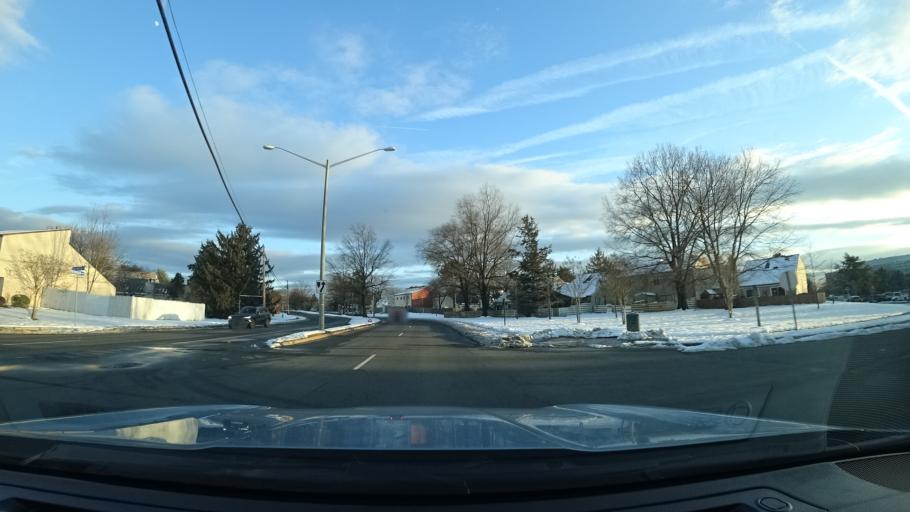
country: US
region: Virginia
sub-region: Fairfax County
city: Herndon
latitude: 38.9615
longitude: -77.3977
